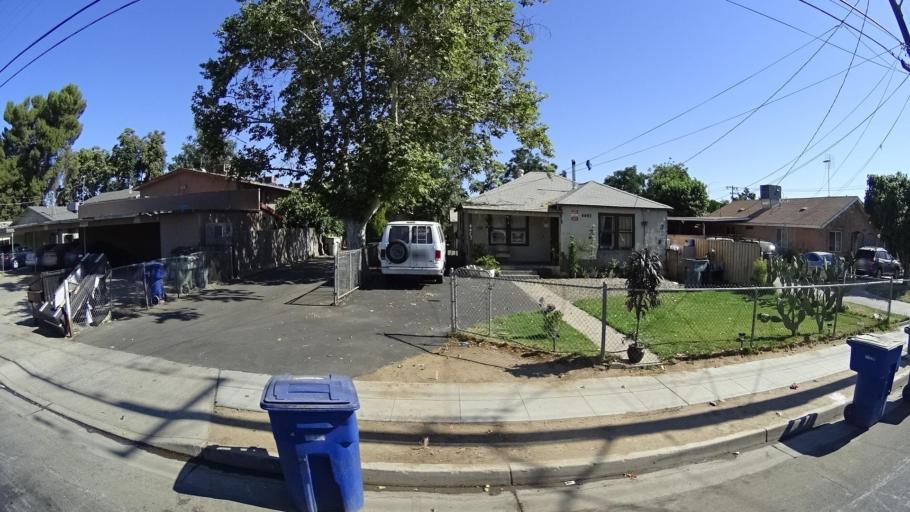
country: US
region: California
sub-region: Fresno County
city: Fresno
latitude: 36.7579
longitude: -119.7508
